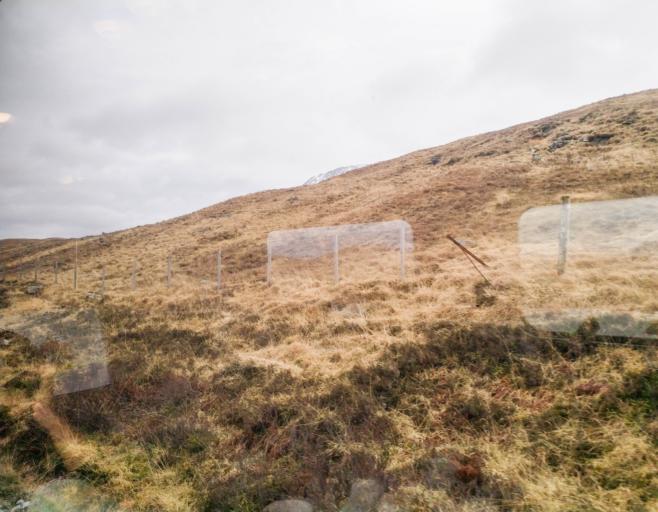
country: GB
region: Scotland
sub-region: Highland
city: Spean Bridge
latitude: 56.5485
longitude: -4.7515
